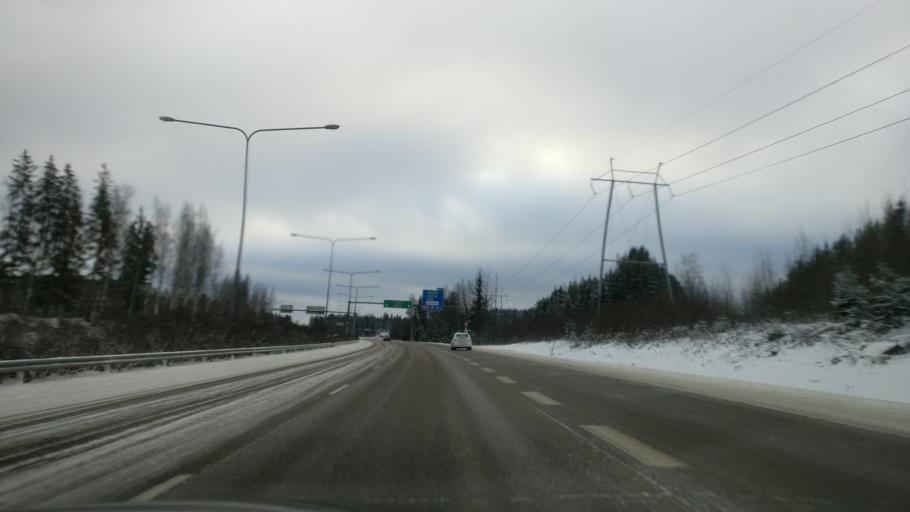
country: FI
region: Paijanne Tavastia
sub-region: Lahti
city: Lahti
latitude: 60.9826
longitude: 25.7326
